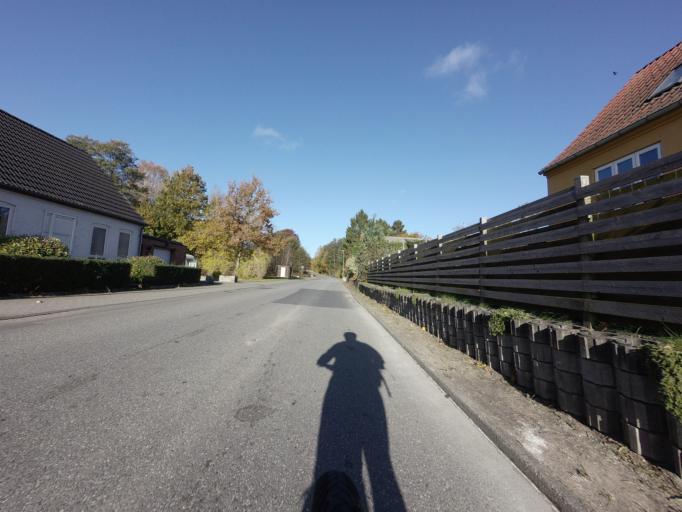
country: DK
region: Central Jutland
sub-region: Syddjurs Kommune
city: Ryomgard
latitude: 56.4121
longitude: 10.5640
